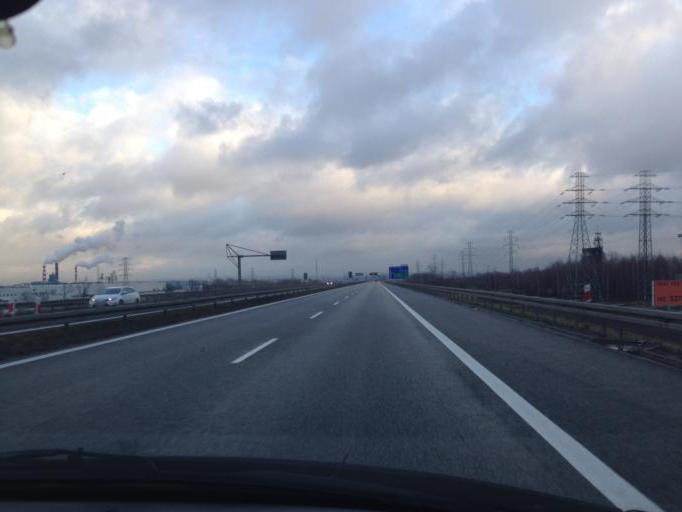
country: PL
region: Silesian Voivodeship
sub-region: Gliwice
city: Gliwice
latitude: 50.2584
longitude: 18.6910
